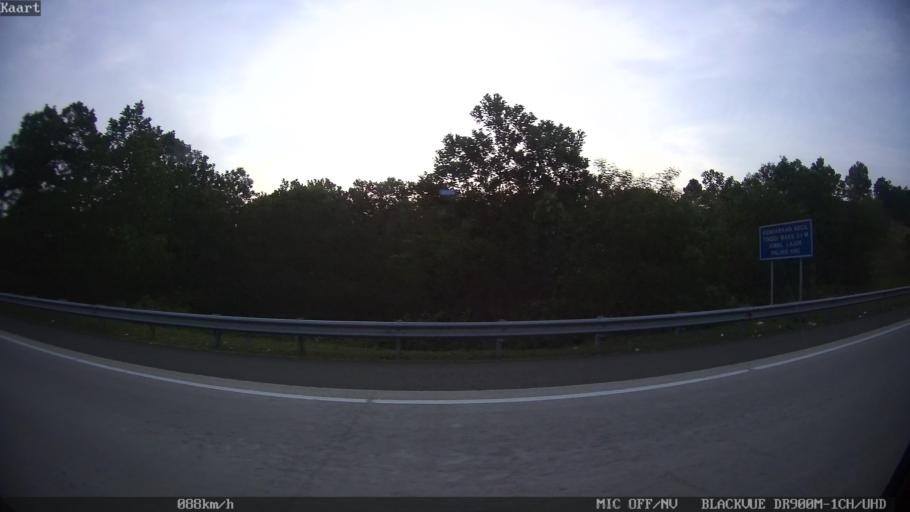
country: ID
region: Lampung
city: Penengahan
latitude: -5.8455
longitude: 105.7270
